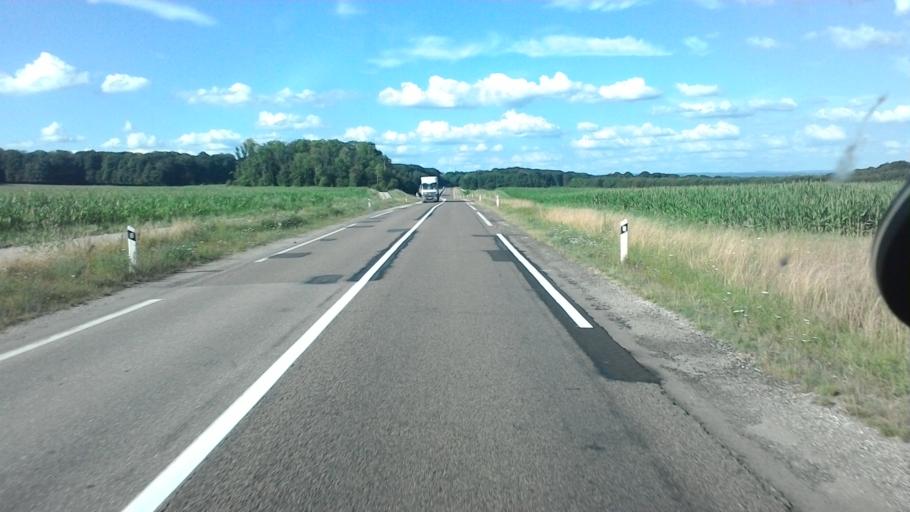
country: FR
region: Franche-Comte
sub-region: Departement de la Haute-Saone
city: Luxeuil-les-Bains
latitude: 47.7352
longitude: 6.3168
